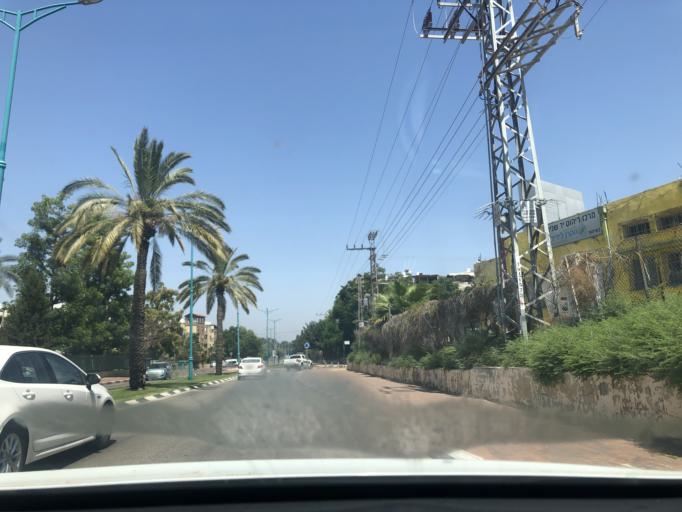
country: IL
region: Central District
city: Lod
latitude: 31.9505
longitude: 34.8975
